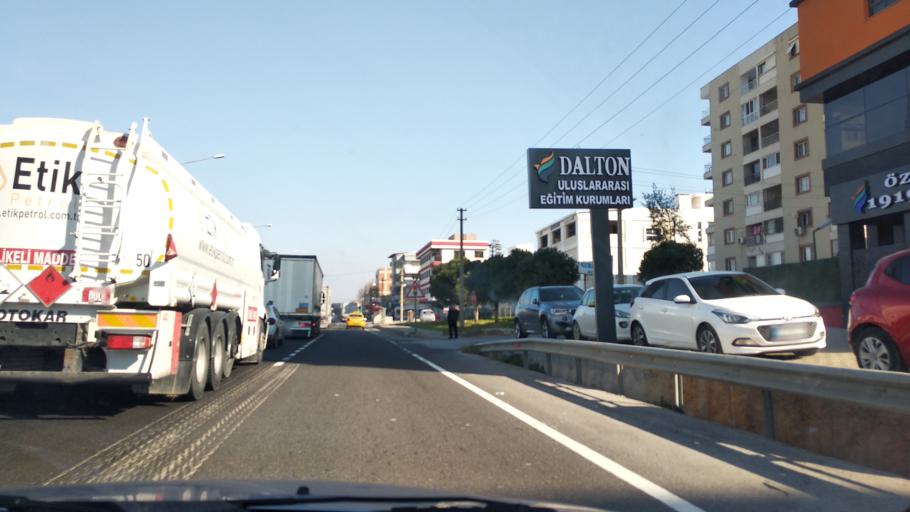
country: TR
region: Izmir
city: Menemen
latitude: 38.5728
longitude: 27.0595
